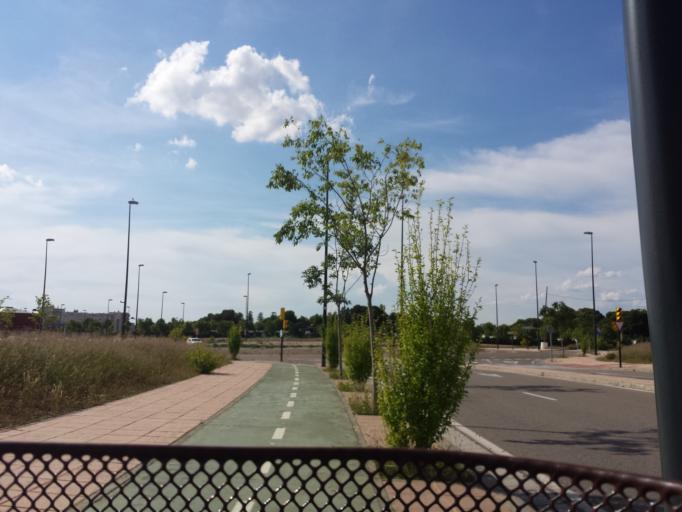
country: ES
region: Aragon
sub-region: Provincia de Zaragoza
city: Montecanal
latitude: 41.6352
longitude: -0.9384
